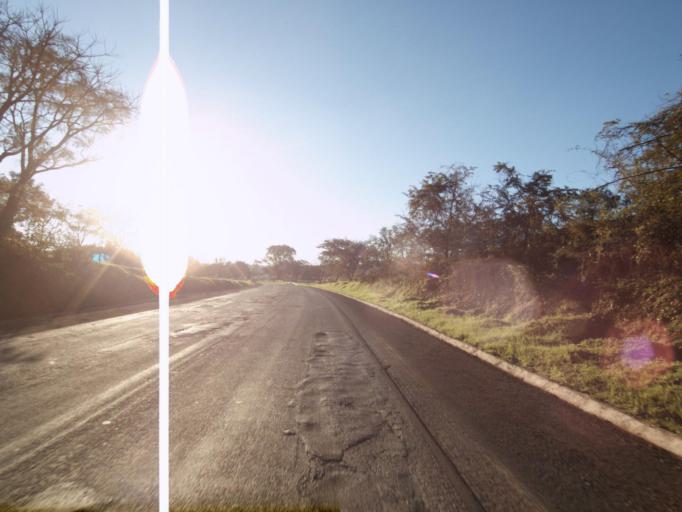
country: BR
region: Santa Catarina
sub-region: Chapeco
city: Chapeco
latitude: -26.8392
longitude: -52.9843
